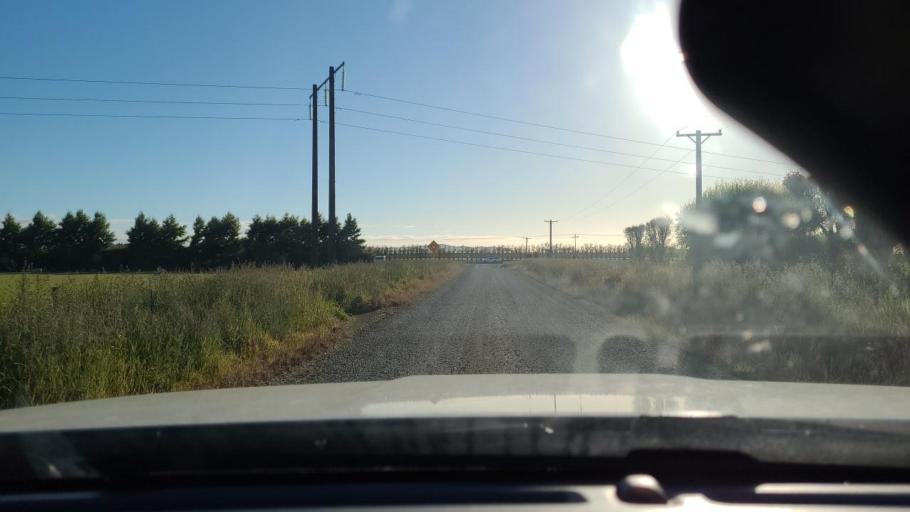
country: NZ
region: Southland
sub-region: Southland District
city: Winton
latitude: -46.2267
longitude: 168.3382
